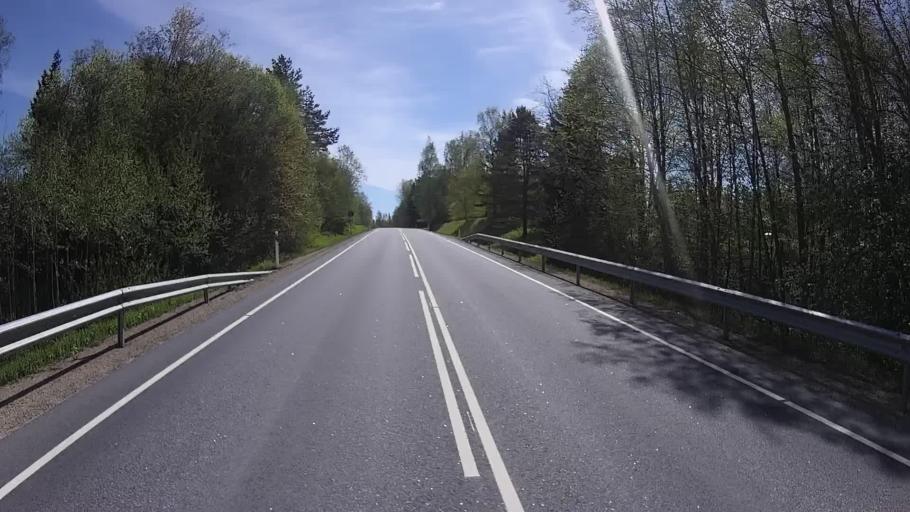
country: EE
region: Polvamaa
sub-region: Polva linn
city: Polva
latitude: 57.9811
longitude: 27.2747
